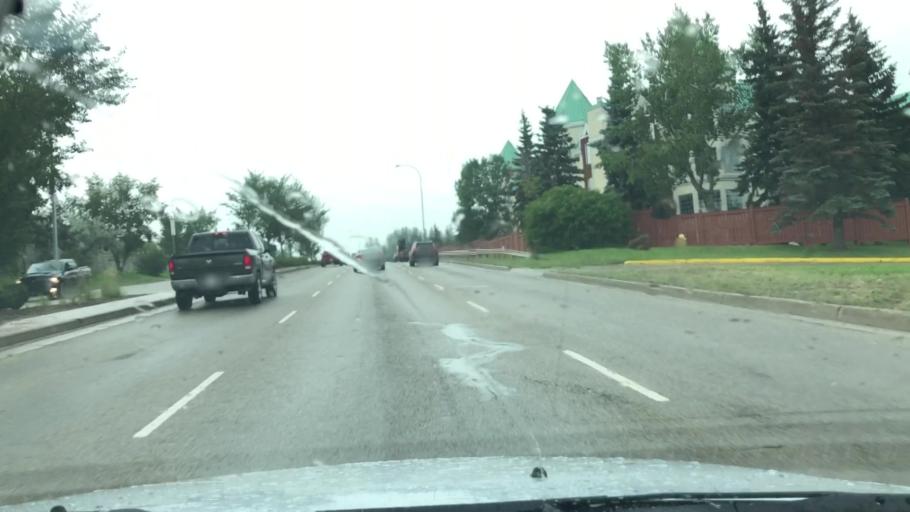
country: CA
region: Alberta
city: St. Albert
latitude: 53.6336
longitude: -113.6230
